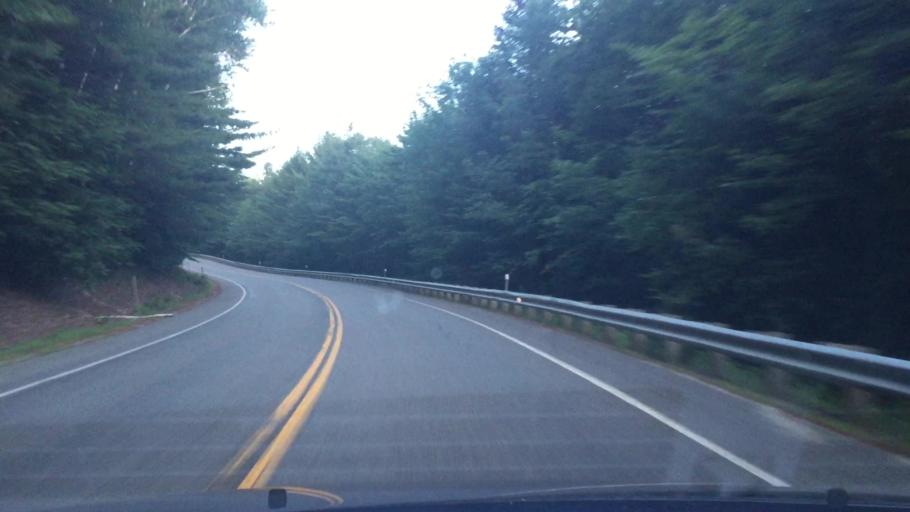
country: US
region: New Hampshire
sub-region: Grafton County
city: Woodstock
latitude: 44.0541
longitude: -71.5828
